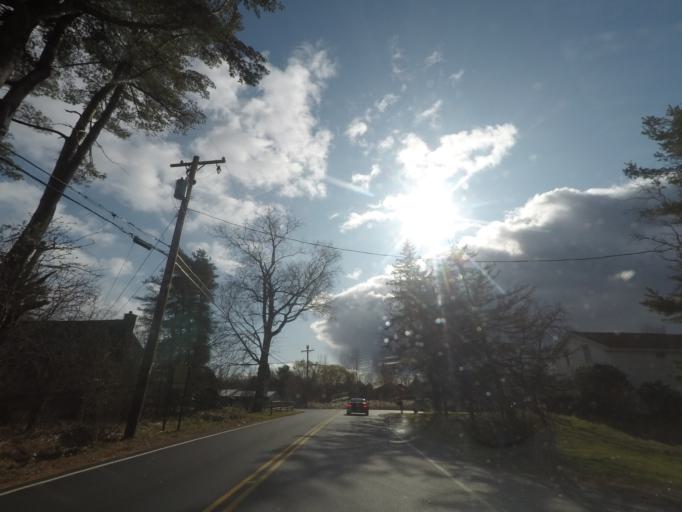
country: US
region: New York
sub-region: Saratoga County
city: Country Knolls
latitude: 42.9271
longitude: -73.8552
